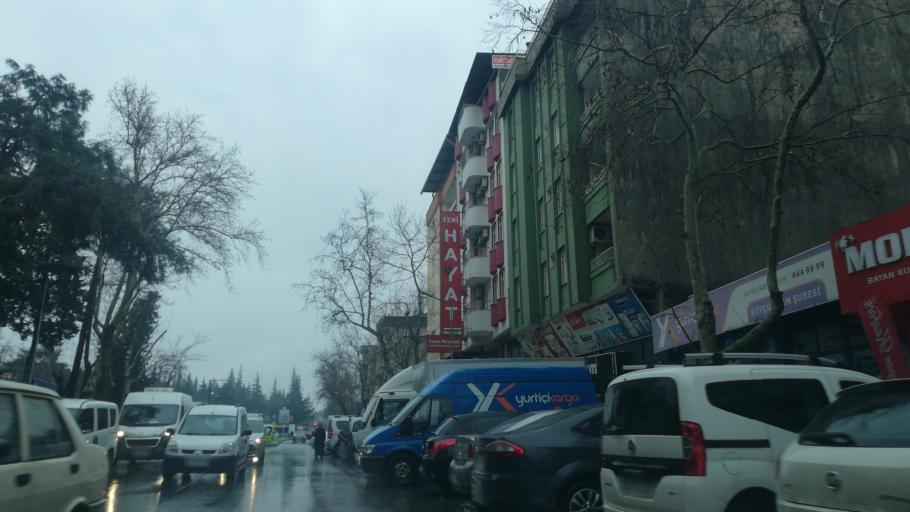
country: TR
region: Kahramanmaras
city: Kahramanmaras
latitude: 37.5792
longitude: 36.9318
